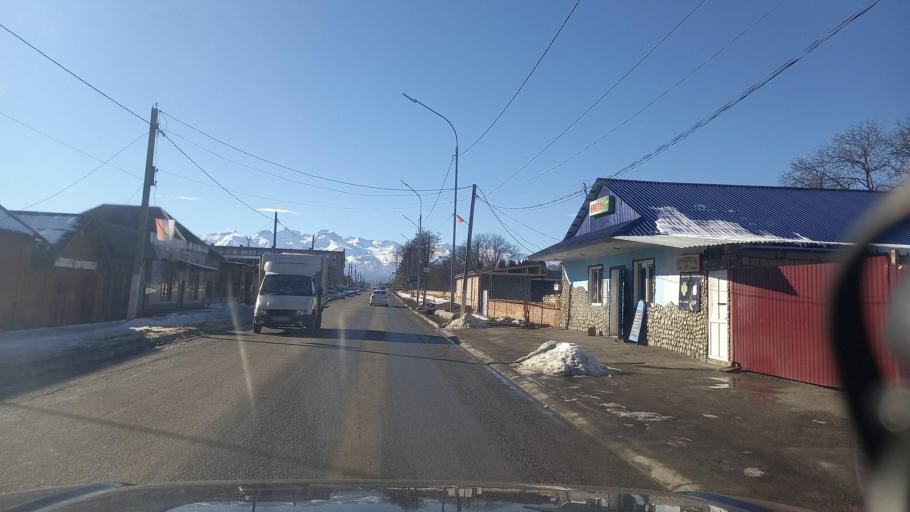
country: RU
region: North Ossetia
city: Chikola
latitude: 43.1993
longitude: 43.9235
